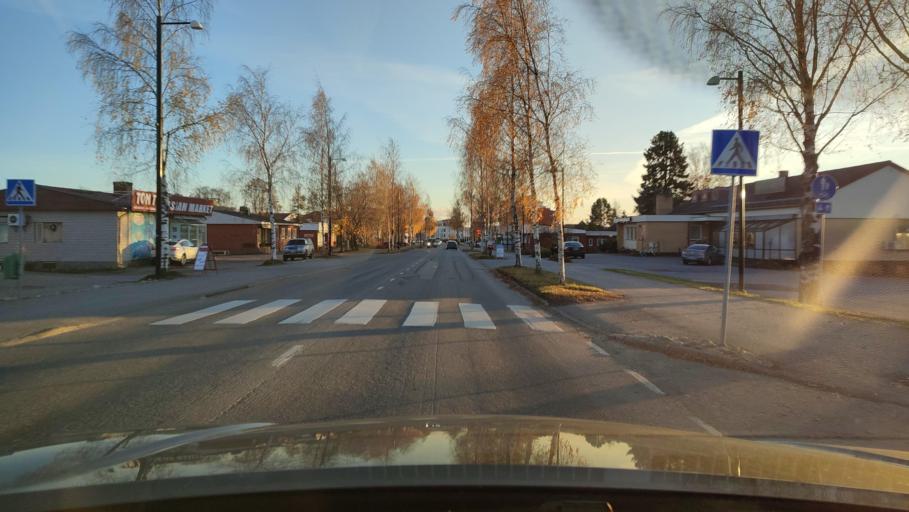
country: FI
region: Ostrobothnia
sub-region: Sydosterbotten
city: Naerpes
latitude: 62.4815
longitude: 21.3382
